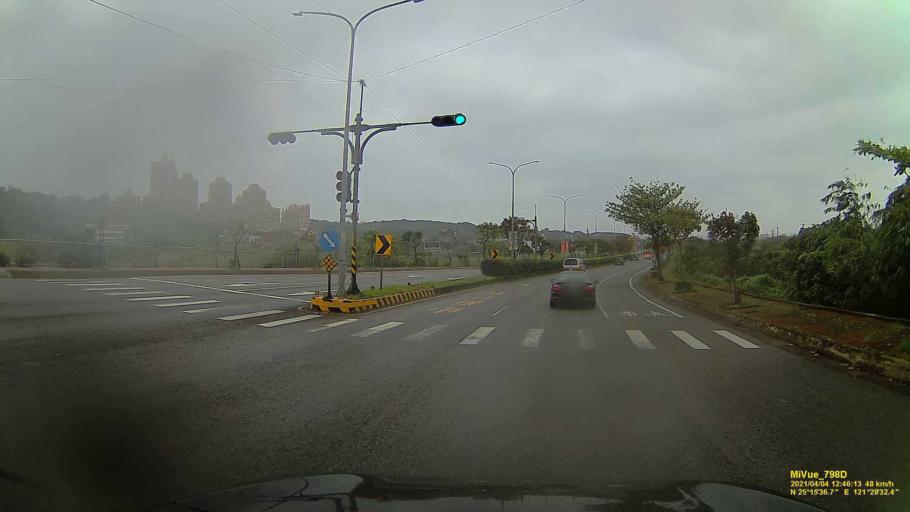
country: TW
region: Taipei
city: Taipei
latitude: 25.2602
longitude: 121.4927
